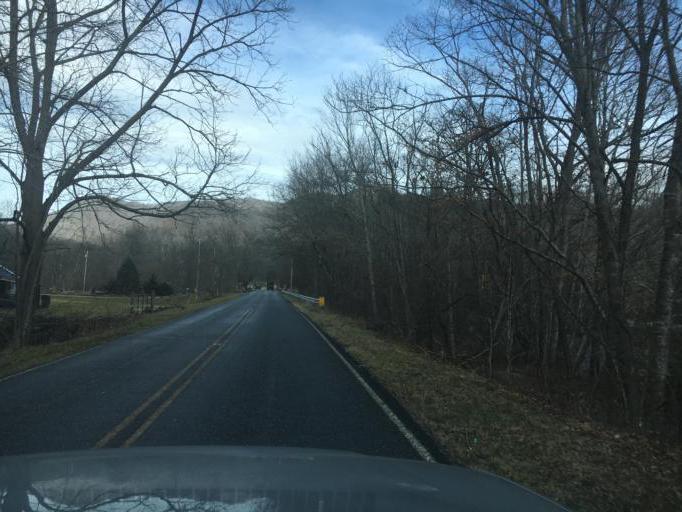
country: US
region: North Carolina
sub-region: Haywood County
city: Canton
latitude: 35.4374
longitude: -82.8141
